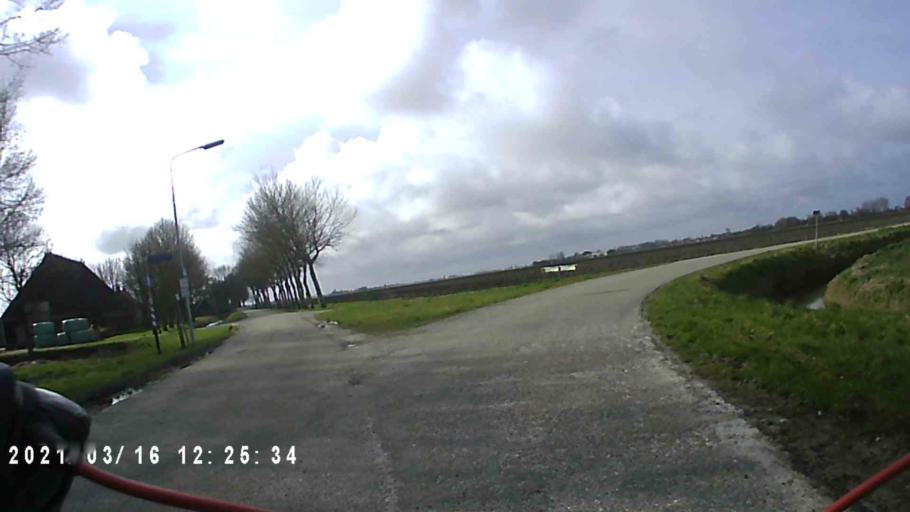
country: NL
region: Friesland
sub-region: Gemeente Leeuwarderadeel
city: Stiens
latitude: 53.2967
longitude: 5.7482
